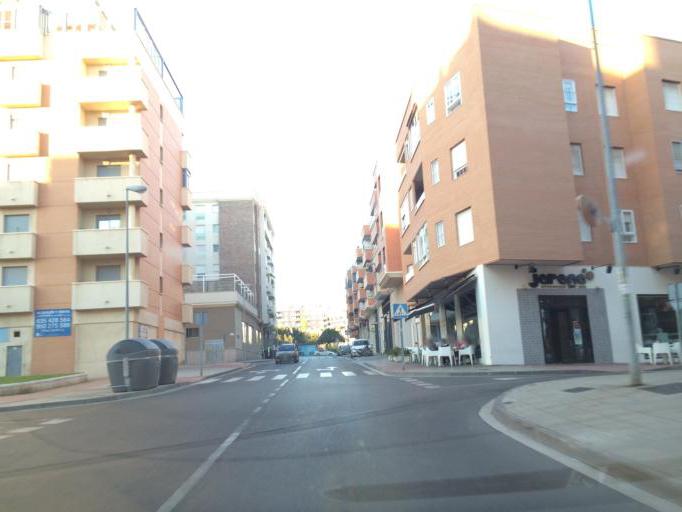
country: ES
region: Andalusia
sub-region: Provincia de Almeria
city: Almeria
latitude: 36.8546
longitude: -2.4450
